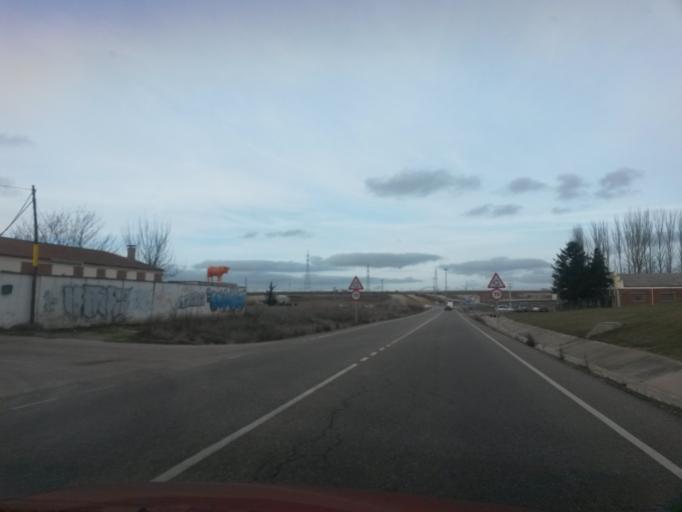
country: ES
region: Castille and Leon
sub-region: Provincia de Salamanca
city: Villares de la Reina
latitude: 40.9953
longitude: -5.6575
